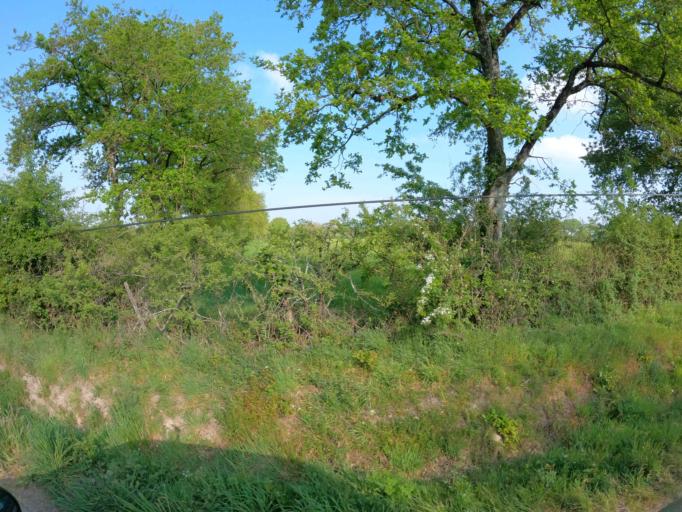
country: FR
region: Pays de la Loire
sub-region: Departement de Maine-et-Loire
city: Torfou
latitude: 47.0484
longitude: -1.0988
